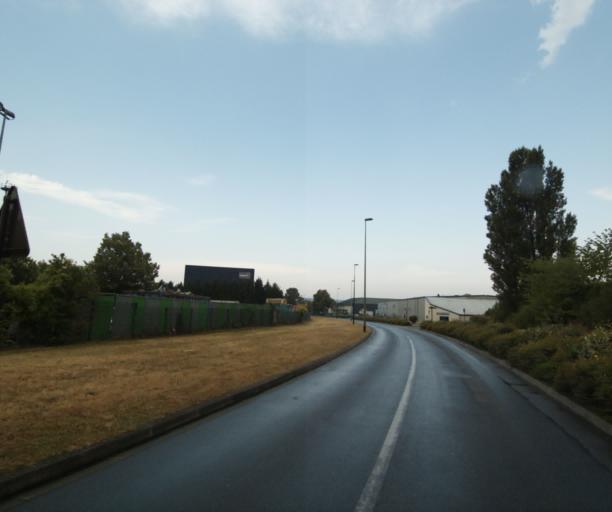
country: FR
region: Ile-de-France
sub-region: Departement des Yvelines
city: Conflans-Sainte-Honorine
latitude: 49.0074
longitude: 2.0823
